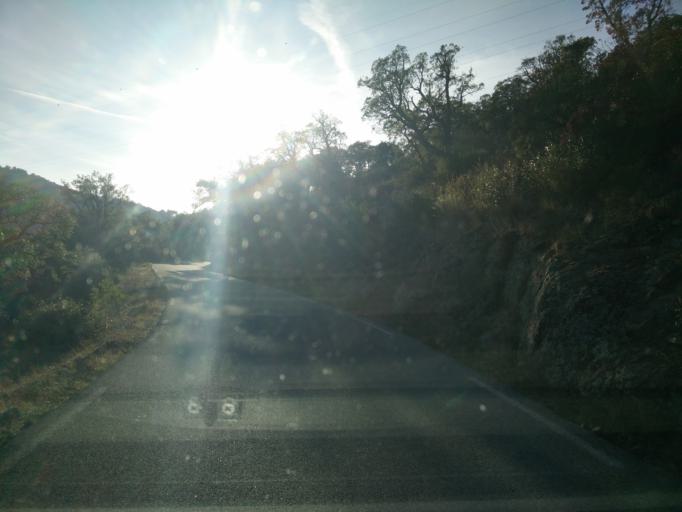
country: FR
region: Provence-Alpes-Cote d'Azur
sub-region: Departement du Var
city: Le Plan-de-la-Tour
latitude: 43.3372
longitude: 6.5154
